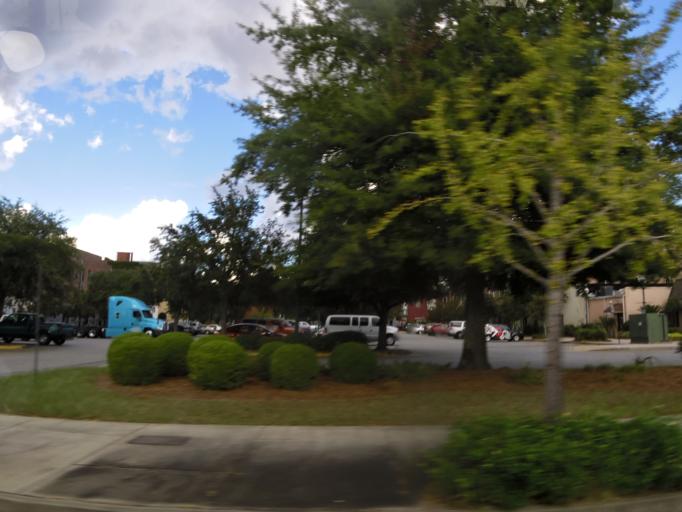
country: US
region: Georgia
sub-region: Lowndes County
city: Valdosta
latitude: 30.8306
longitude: -83.2804
